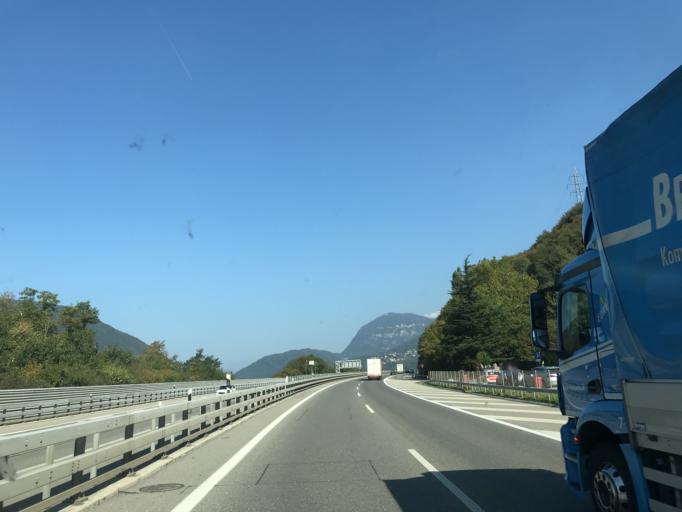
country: CH
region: Ticino
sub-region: Mendrisio District
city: Riva San Vitale
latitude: 45.8926
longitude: 8.9760
